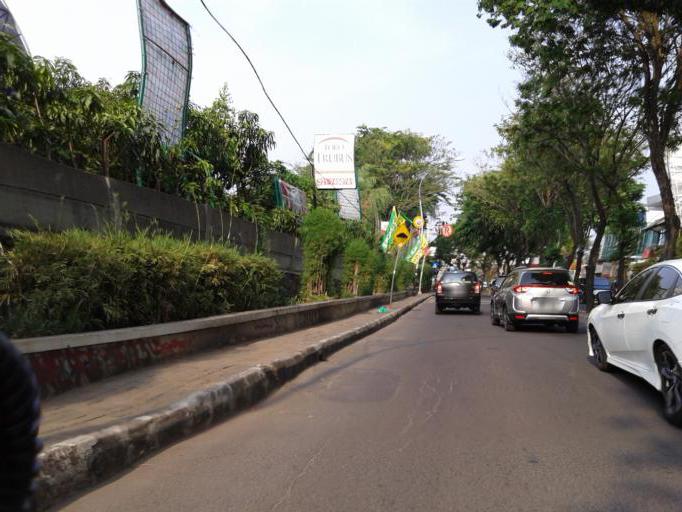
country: ID
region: Banten
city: South Tangerang
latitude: -6.2801
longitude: 106.7162
